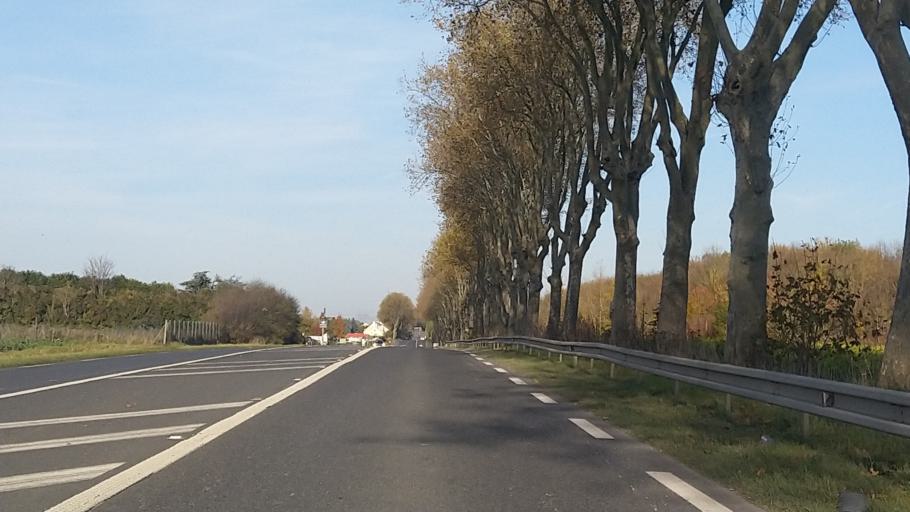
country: FR
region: Ile-de-France
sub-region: Departement du Val-d'Oise
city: Ecouen
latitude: 49.0363
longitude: 2.3932
